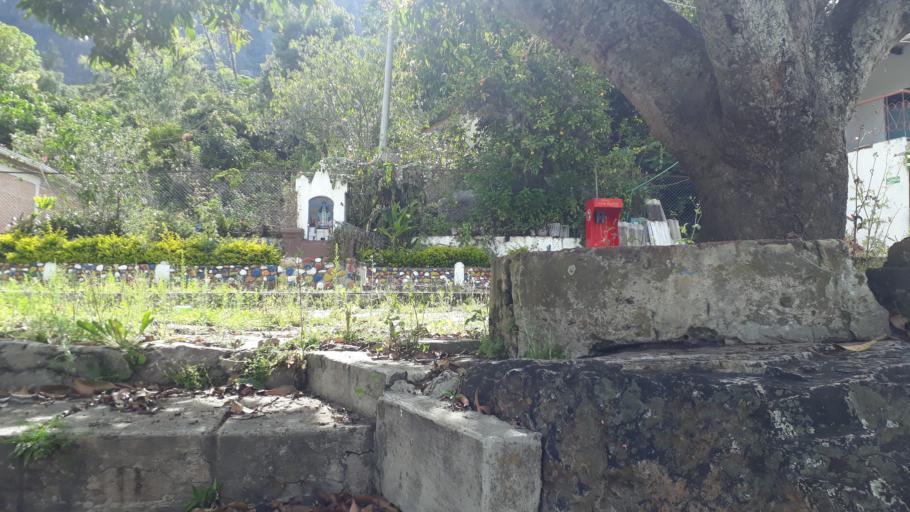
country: CO
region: Boyaca
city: San Mateo
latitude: 6.4070
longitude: -72.5877
